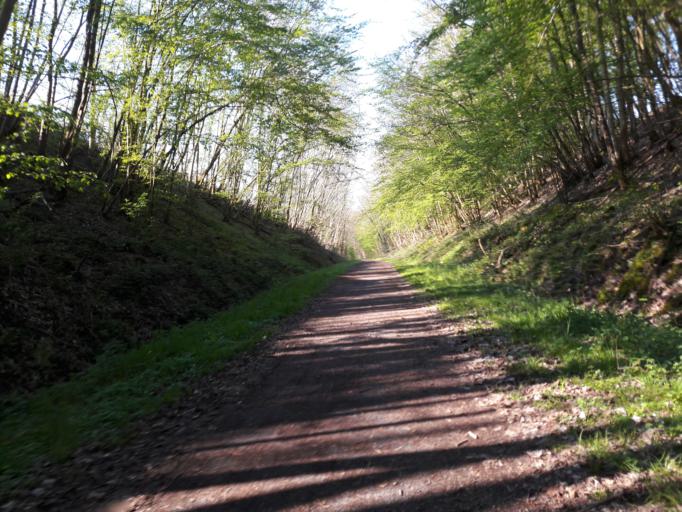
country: FR
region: Nord-Pas-de-Calais
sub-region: Departement du Nord
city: Sains-du-Nord
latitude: 50.1433
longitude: 4.0679
